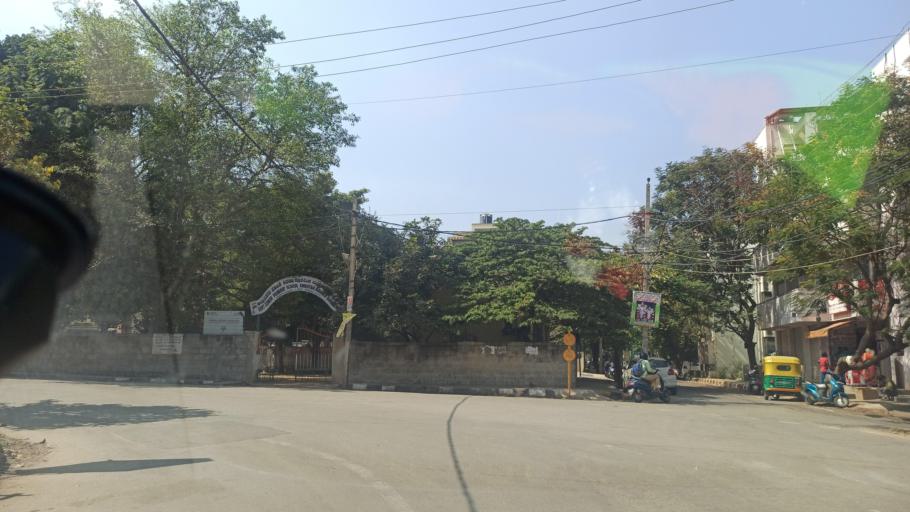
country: IN
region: Karnataka
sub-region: Bangalore Urban
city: Yelahanka
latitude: 13.0589
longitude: 77.5990
